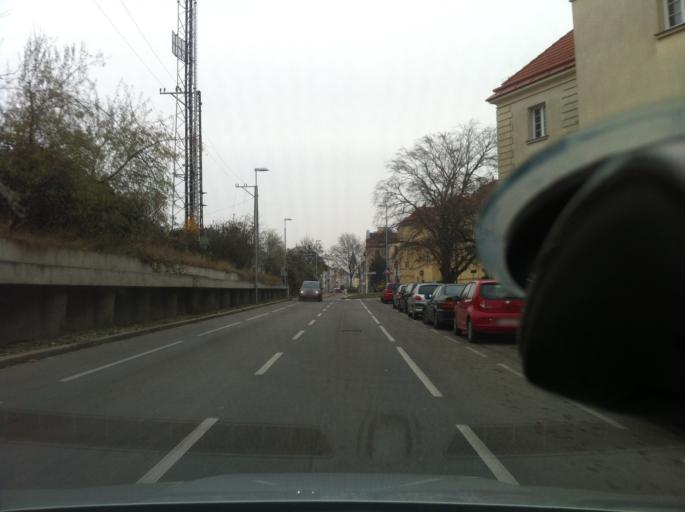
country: AT
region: Lower Austria
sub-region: Politischer Bezirk Modling
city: Perchtoldsdorf
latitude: 48.1923
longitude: 16.2943
